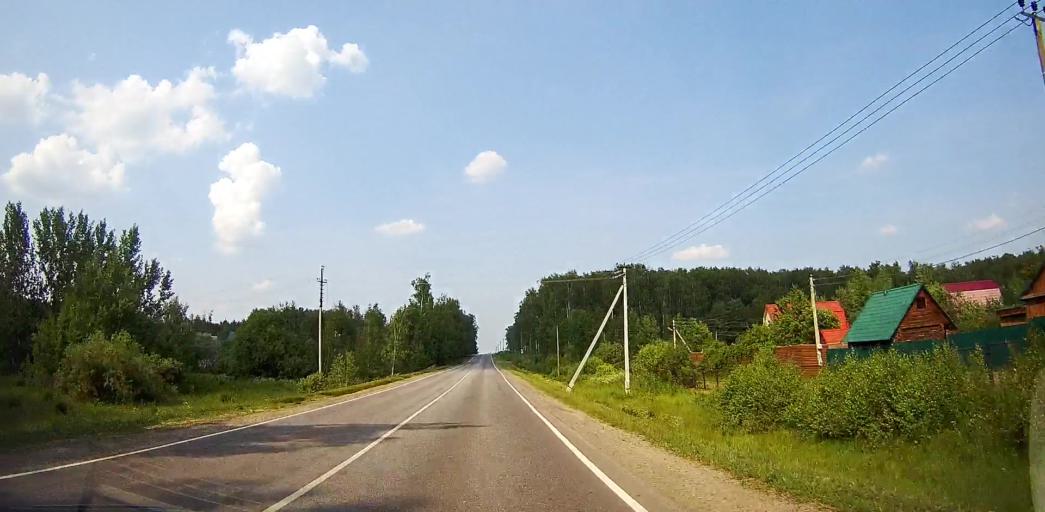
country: RU
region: Moskovskaya
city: Mikhnevo
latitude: 55.1673
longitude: 37.9599
